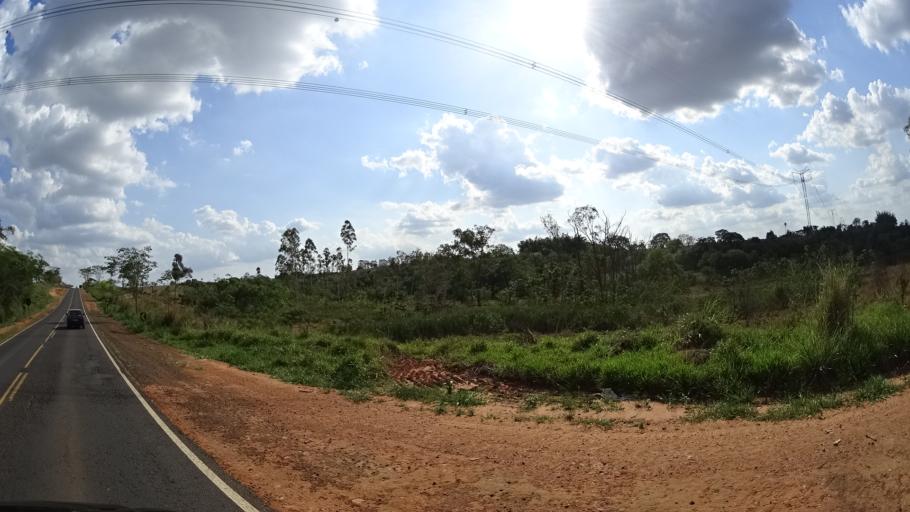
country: BR
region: Sao Paulo
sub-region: Urupes
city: Urupes
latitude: -21.1459
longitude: -49.2818
